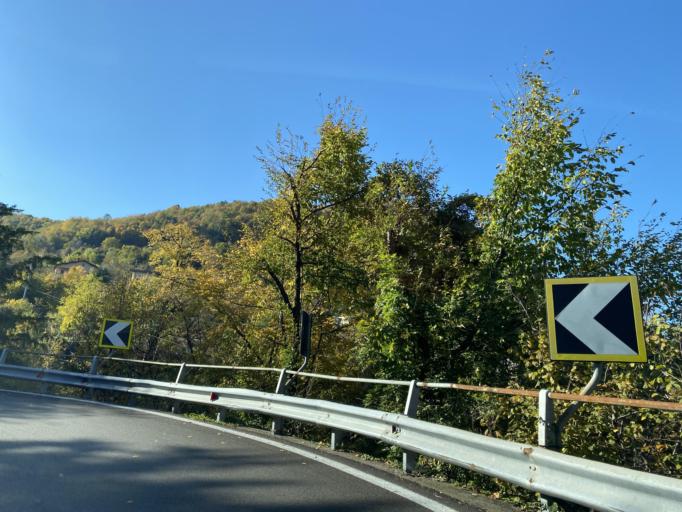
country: IT
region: Lombardy
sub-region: Provincia di Como
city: Osteno
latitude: 46.0059
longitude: 9.0850
